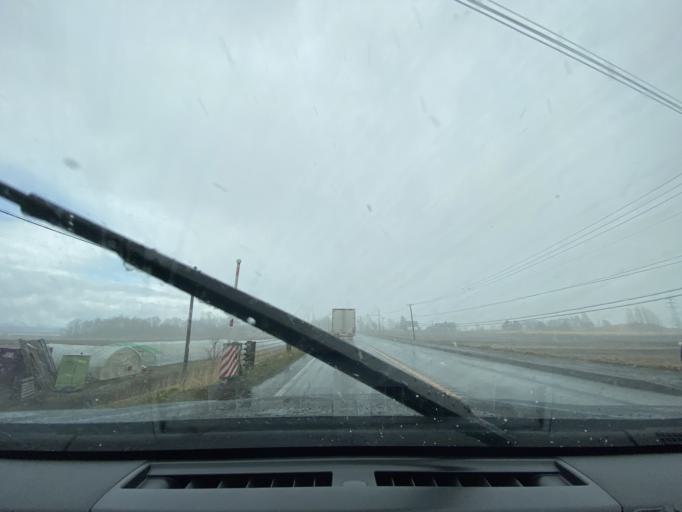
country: JP
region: Hokkaido
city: Fukagawa
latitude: 43.6464
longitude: 141.9592
